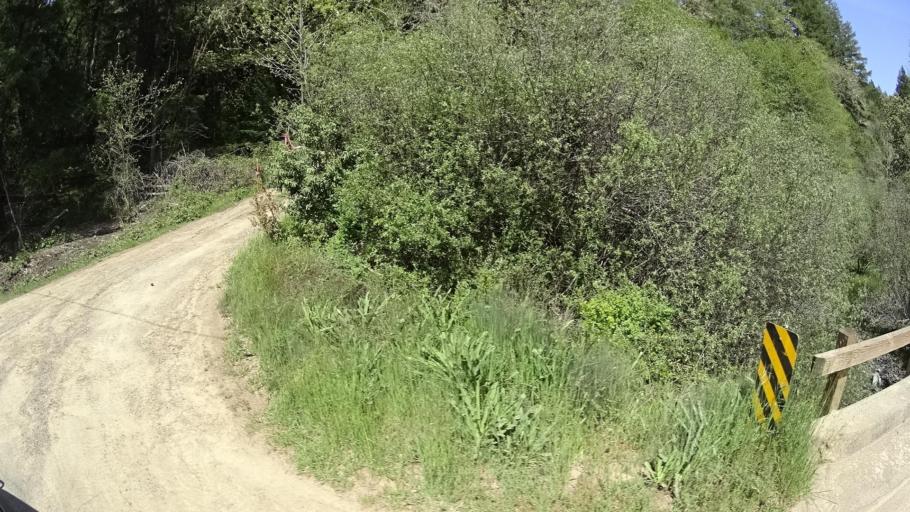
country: US
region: California
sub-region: Humboldt County
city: Redway
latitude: 40.3096
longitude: -123.6555
